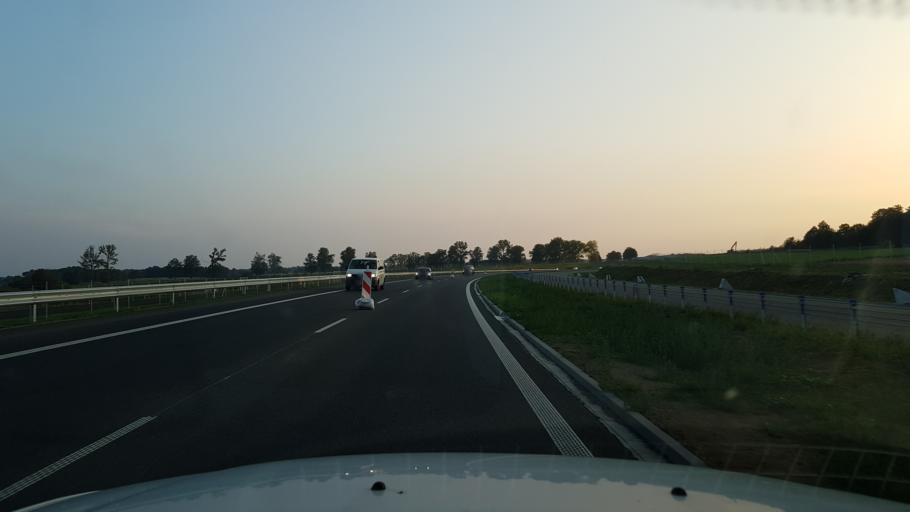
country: PL
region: West Pomeranian Voivodeship
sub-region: Powiat goleniowski
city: Nowogard
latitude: 53.7168
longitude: 15.1926
